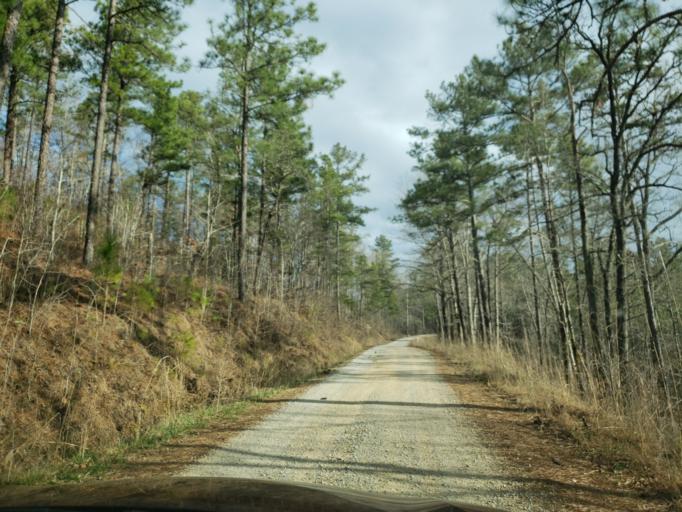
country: US
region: Alabama
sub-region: Cleburne County
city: Heflin
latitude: 33.6523
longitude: -85.6338
